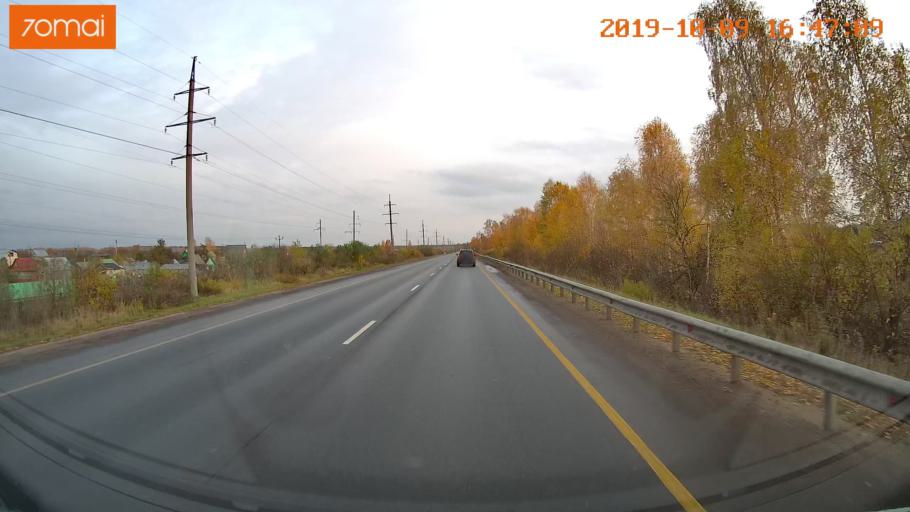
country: RU
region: Kostroma
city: Volgorechensk
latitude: 57.4390
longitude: 41.1737
